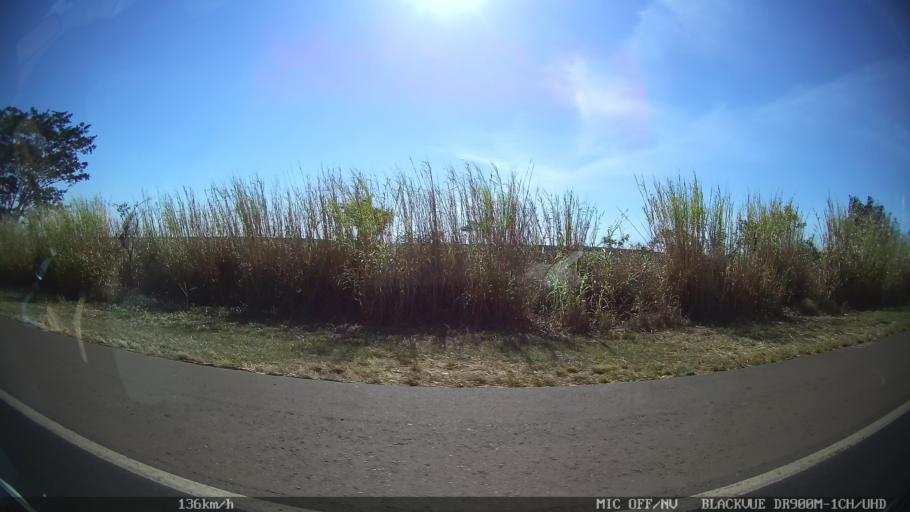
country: BR
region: Sao Paulo
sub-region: Olimpia
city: Olimpia
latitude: -20.6757
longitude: -48.8853
